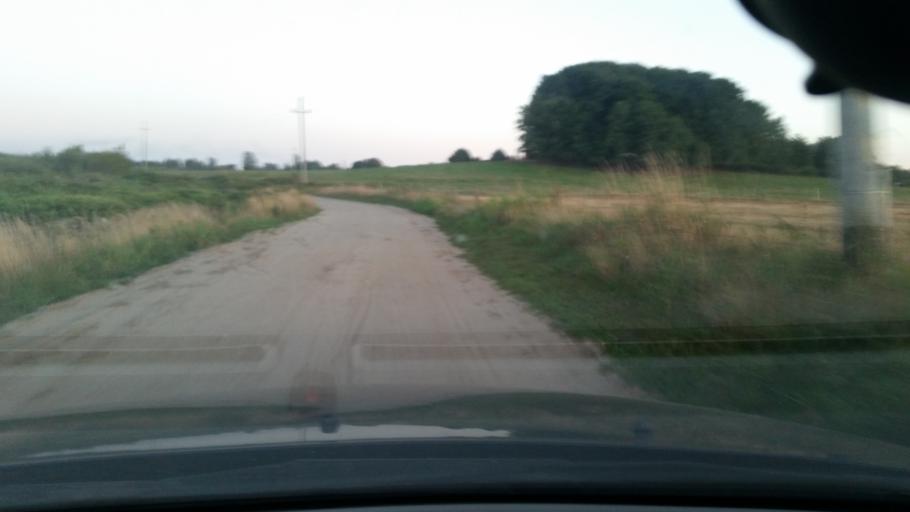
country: PL
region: Pomeranian Voivodeship
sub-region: Powiat wejherowski
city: Choczewo
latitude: 54.7740
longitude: 17.7942
